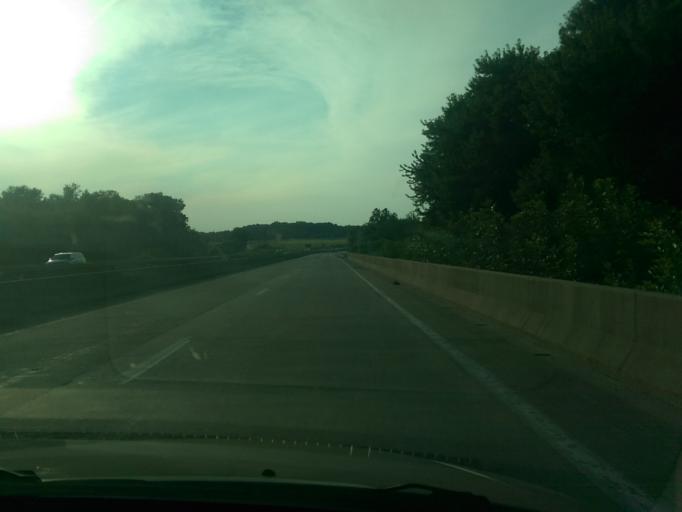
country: US
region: Missouri
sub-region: Platte County
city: Platte City
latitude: 39.3797
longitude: -94.7837
